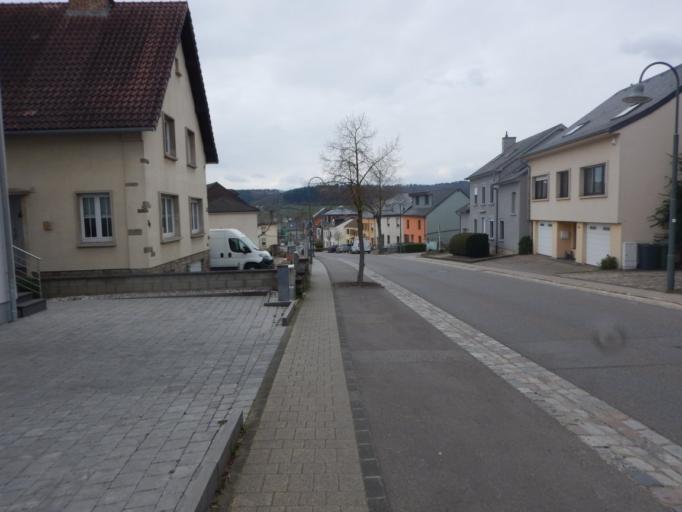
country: LU
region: Luxembourg
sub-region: Canton de Mersch
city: Lorentzweiler
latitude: 49.7023
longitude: 6.1440
